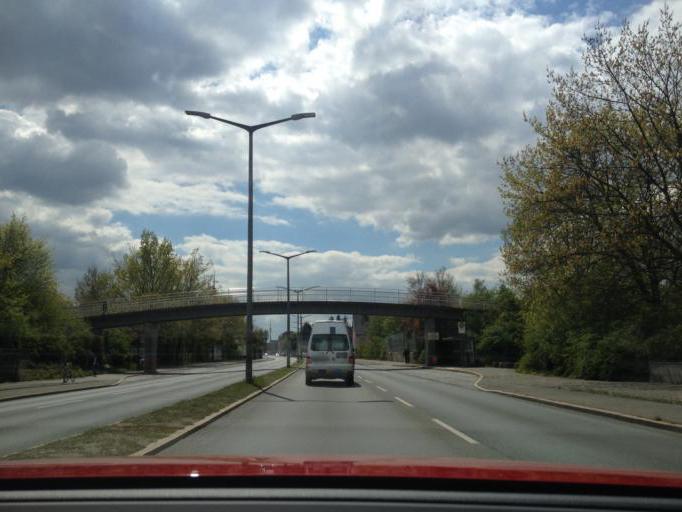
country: DE
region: Bavaria
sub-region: Regierungsbezirk Mittelfranken
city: Grossreuth bei Schweinau
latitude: 49.4457
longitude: 11.0358
